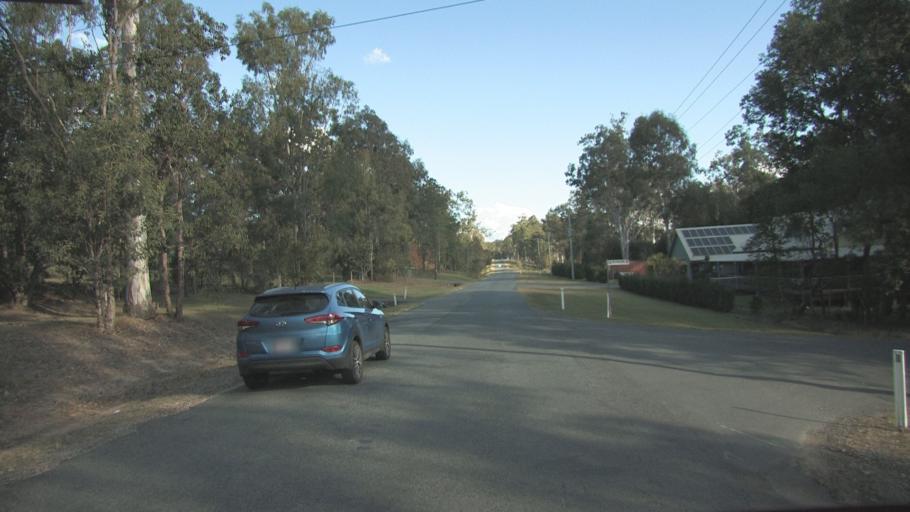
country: AU
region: Queensland
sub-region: Ipswich
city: Springfield Lakes
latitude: -27.7414
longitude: 152.9424
